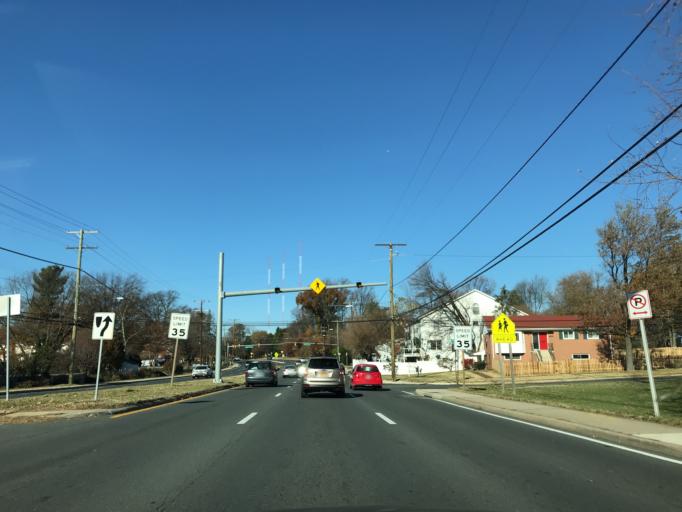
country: US
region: Maryland
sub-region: Montgomery County
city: Wheaton
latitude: 39.0389
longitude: -77.0415
